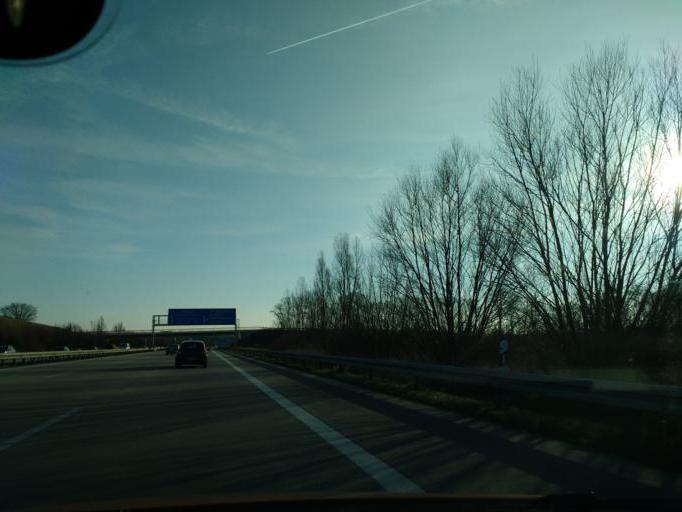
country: DE
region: Brandenburg
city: Ahrensfelde
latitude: 52.6065
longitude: 13.5954
